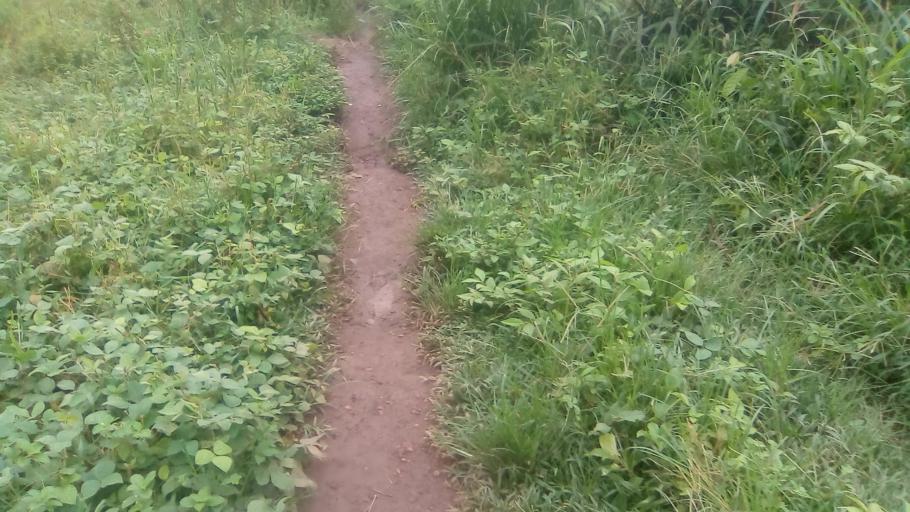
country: SL
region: Southern Province
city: Moyamba
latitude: 8.1599
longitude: -12.4290
